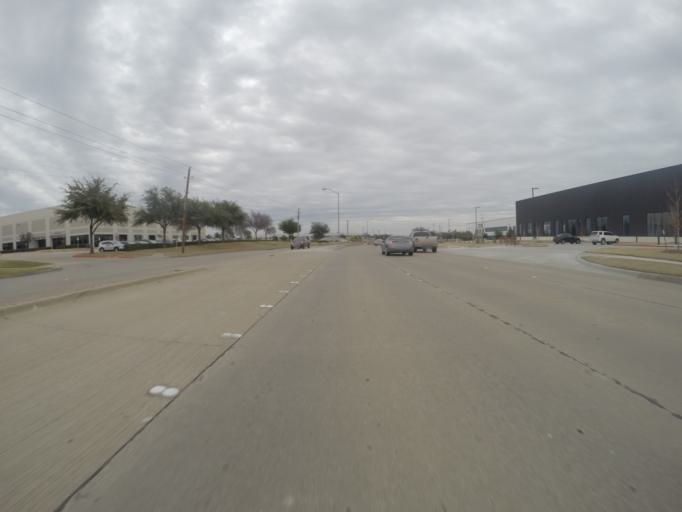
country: US
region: Texas
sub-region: Collin County
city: Saint Paul
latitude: 33.0420
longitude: -96.5622
